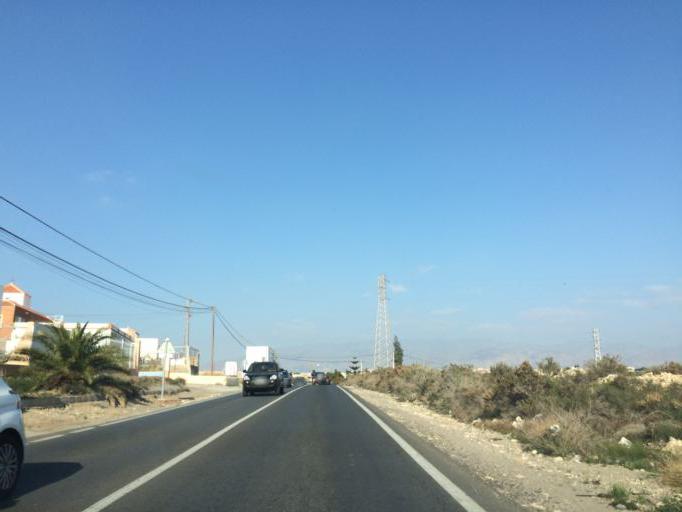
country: ES
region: Andalusia
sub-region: Provincia de Almeria
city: Huercal de Almeria
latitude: 36.8571
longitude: -2.4200
